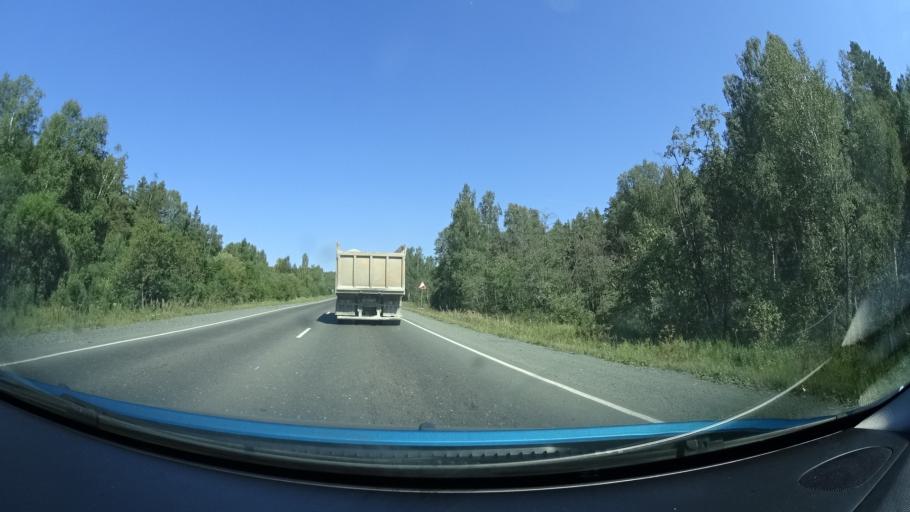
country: RU
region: Bashkortostan
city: Abzakovo
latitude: 53.8725
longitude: 58.5363
